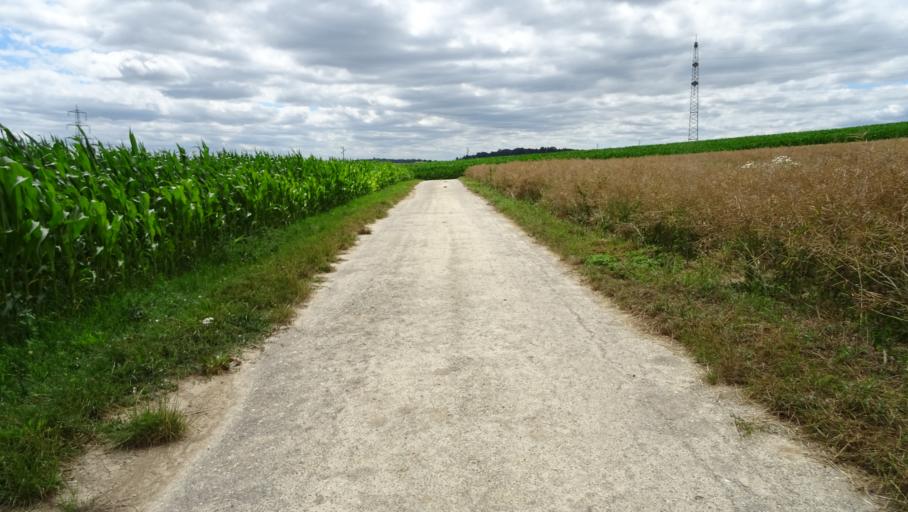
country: DE
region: Baden-Wuerttemberg
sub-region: Karlsruhe Region
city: Neunkirchen
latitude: 49.3830
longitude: 9.0257
